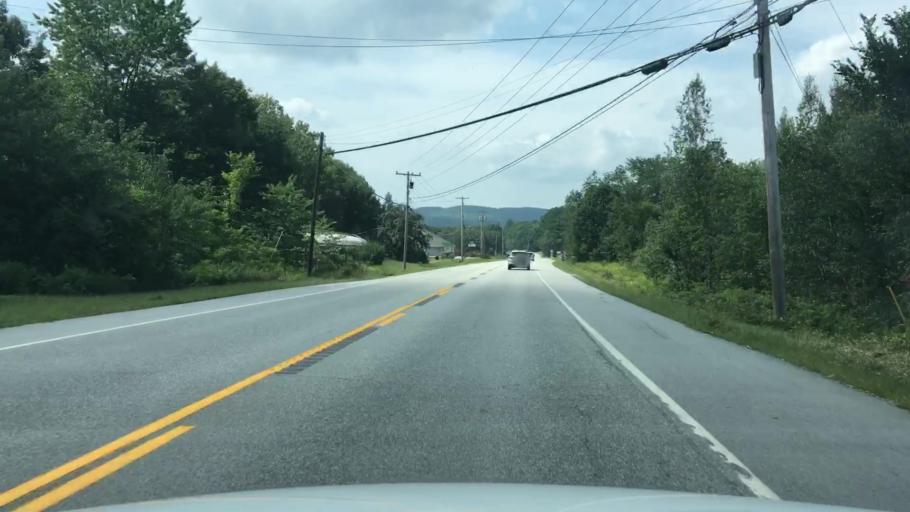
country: US
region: Maine
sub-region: Oxford County
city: Rumford
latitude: 44.5093
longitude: -70.5808
